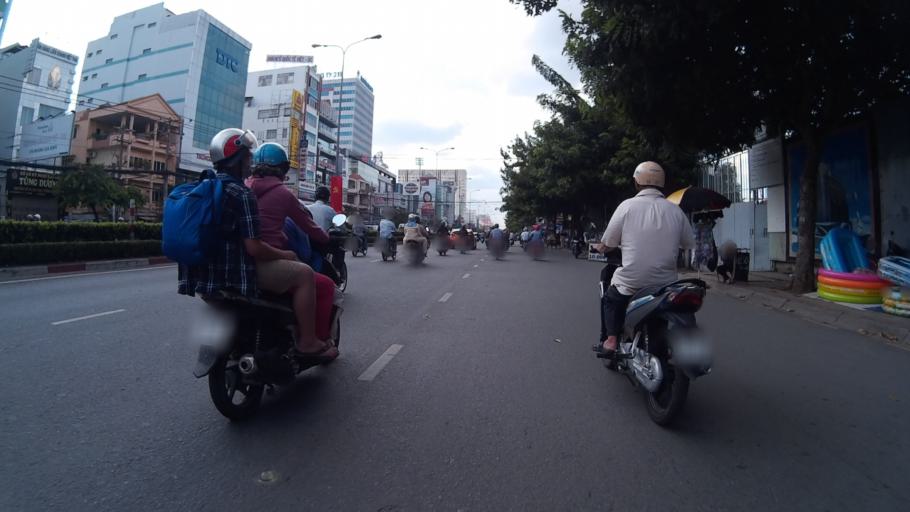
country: VN
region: Ho Chi Minh City
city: Quan Phu Nhuan
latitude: 10.8014
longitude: 106.6553
